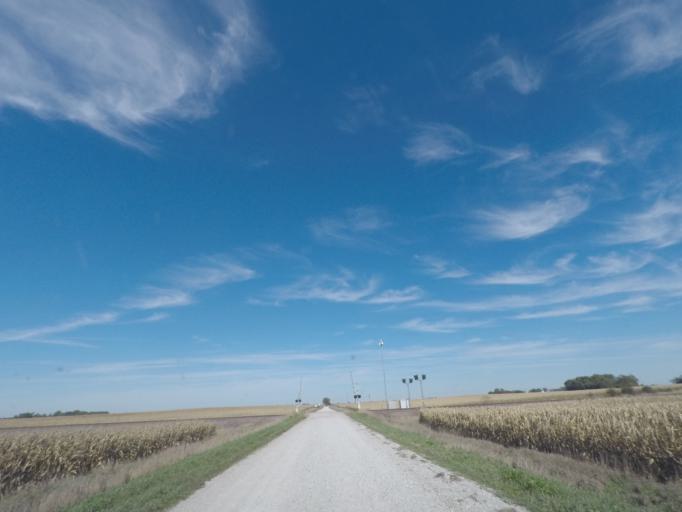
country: US
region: Iowa
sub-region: Story County
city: Nevada
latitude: 42.0184
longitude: -93.3573
